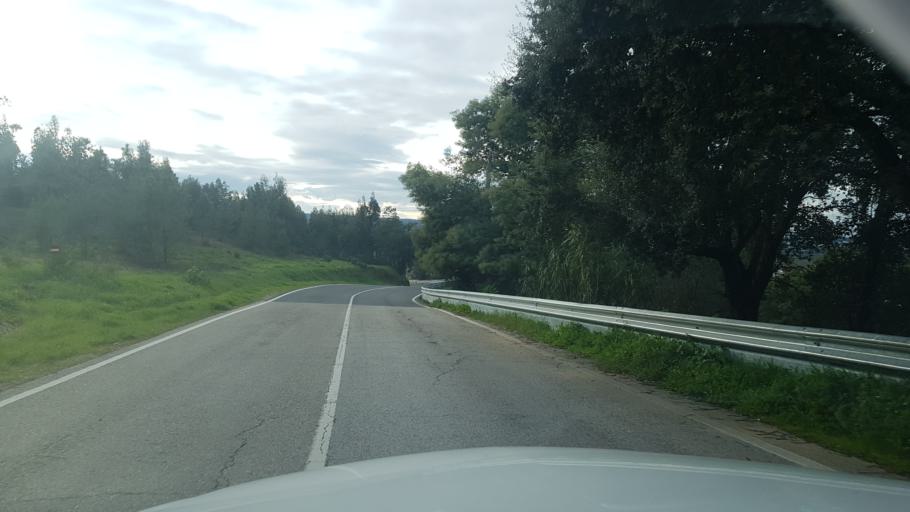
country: PT
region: Santarem
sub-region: Abrantes
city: Tramagal
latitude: 39.4747
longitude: -8.2350
